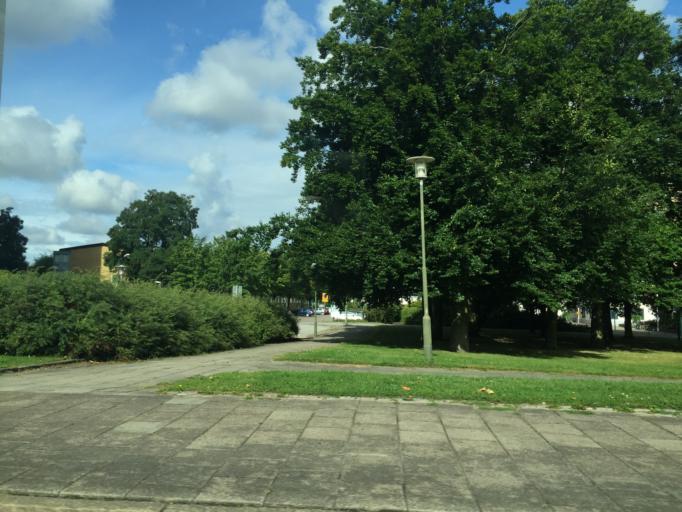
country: SE
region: Skane
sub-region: Malmo
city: Malmoe
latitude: 55.5825
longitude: 12.9982
